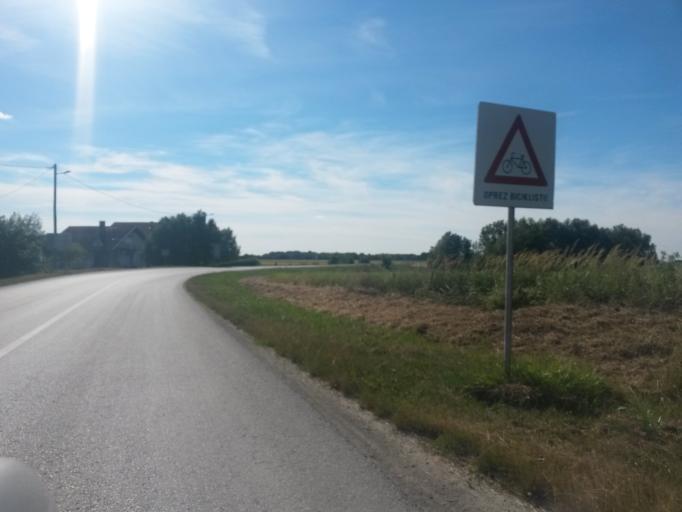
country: HR
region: Osjecko-Baranjska
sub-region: Grad Osijek
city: Bilje
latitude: 45.5995
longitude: 18.7800
